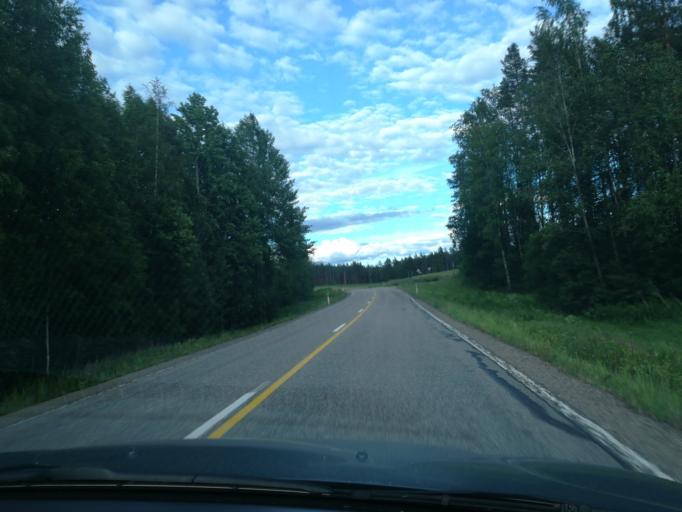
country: FI
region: Southern Savonia
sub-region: Mikkeli
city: Puumala
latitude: 61.5008
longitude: 27.8567
